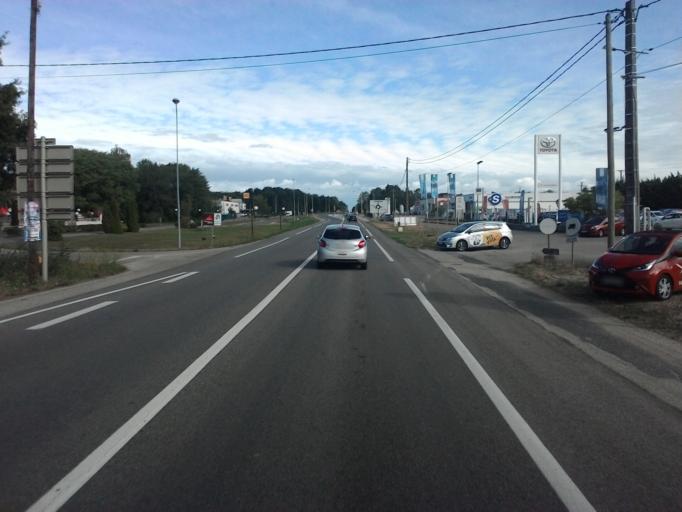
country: FR
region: Rhone-Alpes
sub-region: Departement de l'Ain
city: Montagnat
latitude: 46.1738
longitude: 5.2592
